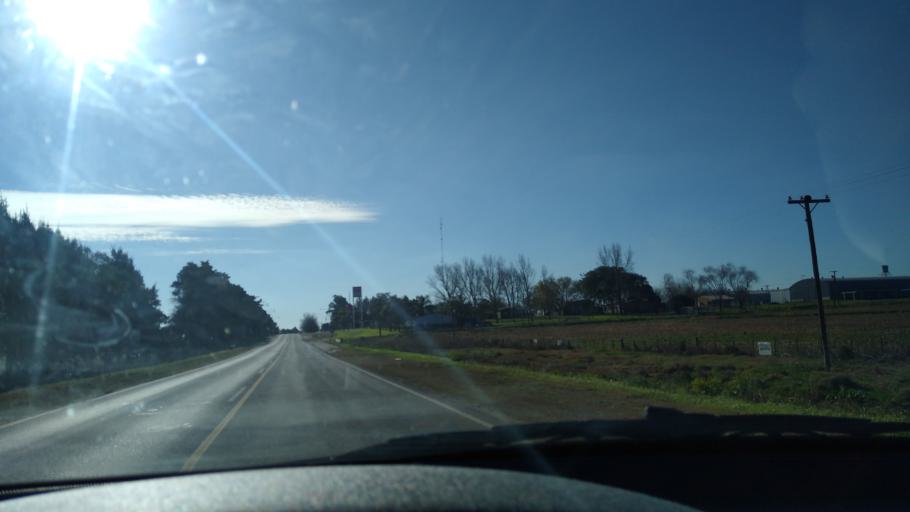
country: AR
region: Entre Rios
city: Aranguren
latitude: -32.4241
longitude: -60.3127
